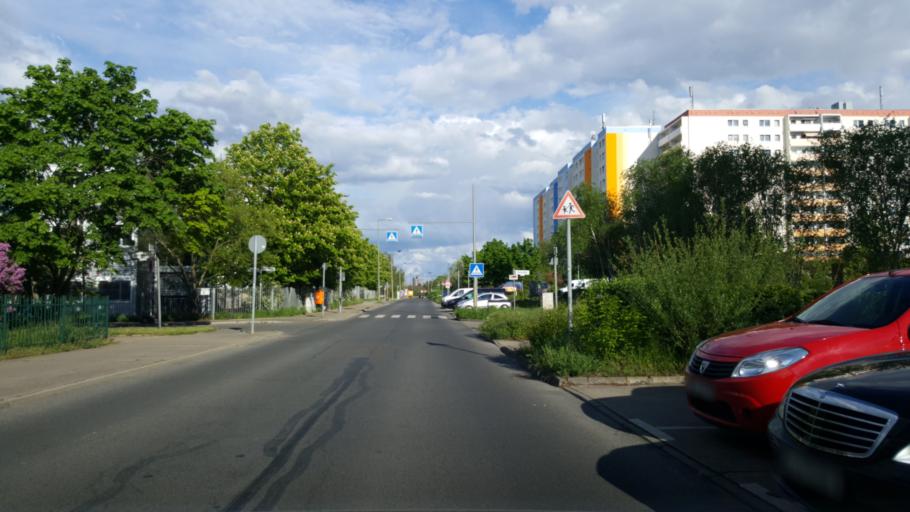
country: DE
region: Berlin
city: Altglienicke
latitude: 52.4061
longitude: 13.5272
